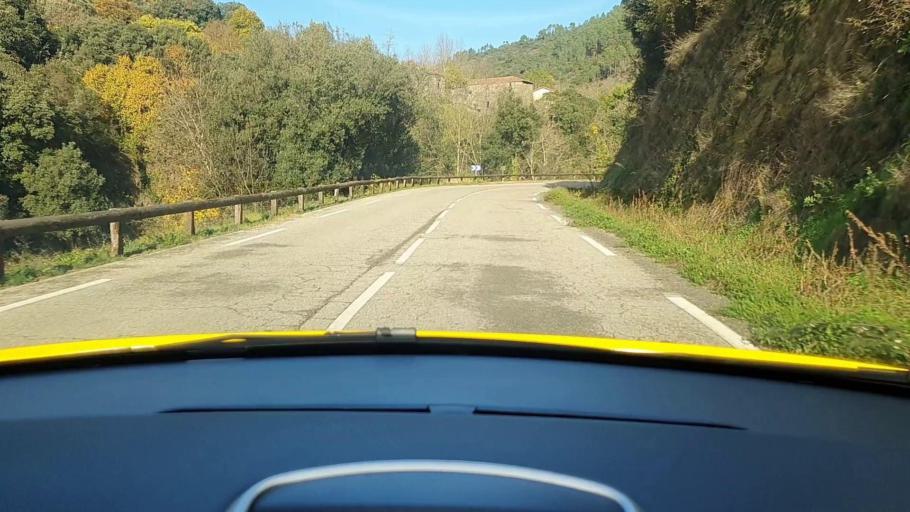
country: FR
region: Languedoc-Roussillon
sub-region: Departement du Gard
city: Valleraugue
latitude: 44.1432
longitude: 3.6987
